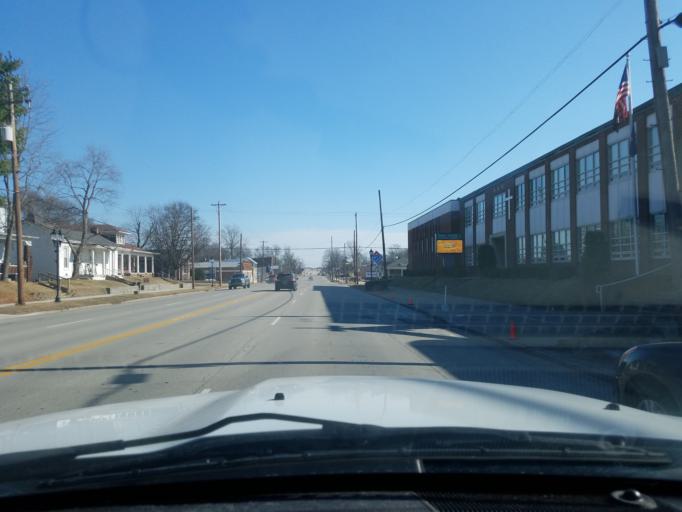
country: US
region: Kentucky
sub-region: Henderson County
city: Henderson
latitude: 37.8381
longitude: -87.5851
